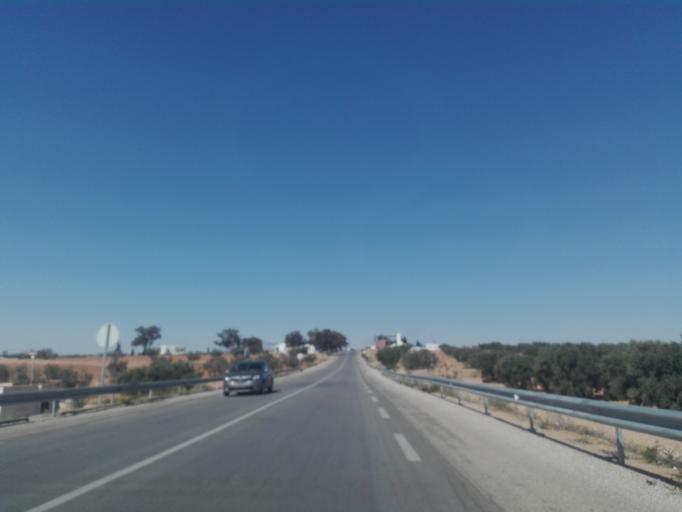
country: TN
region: Safaqis
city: Bi'r `Ali Bin Khalifah
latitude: 34.7412
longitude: 10.3762
